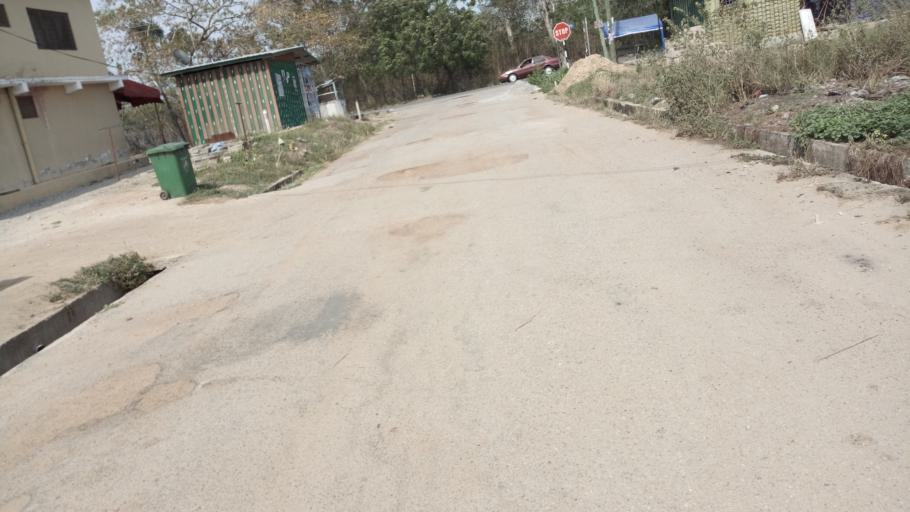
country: GH
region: Central
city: Winneba
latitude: 5.3634
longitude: -0.6357
